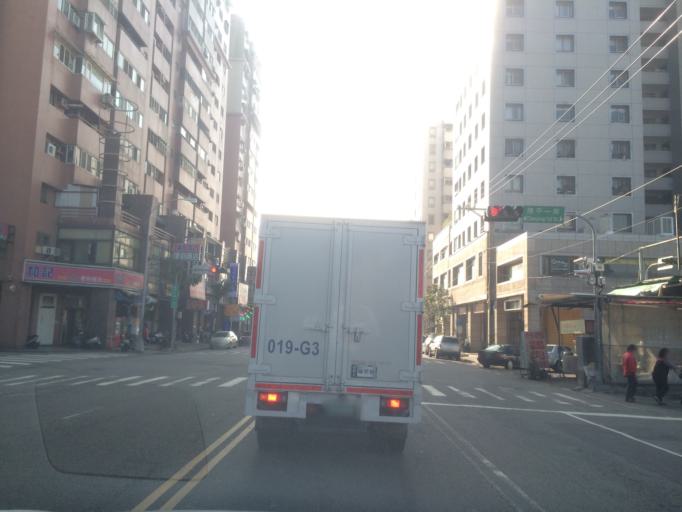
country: TW
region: Taiwan
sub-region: Taichung City
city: Taichung
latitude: 24.1869
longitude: 120.6663
